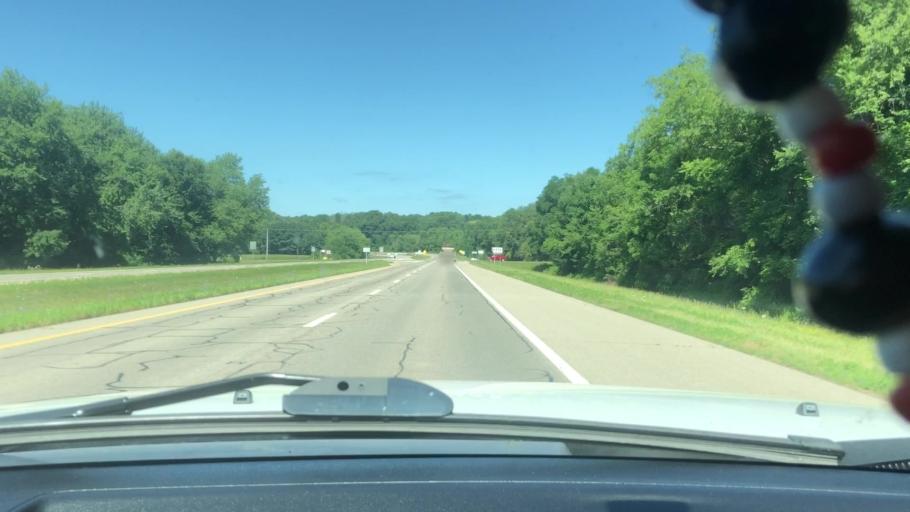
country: US
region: Ohio
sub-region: Coshocton County
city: West Lafayette
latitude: 40.2868
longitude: -81.6815
